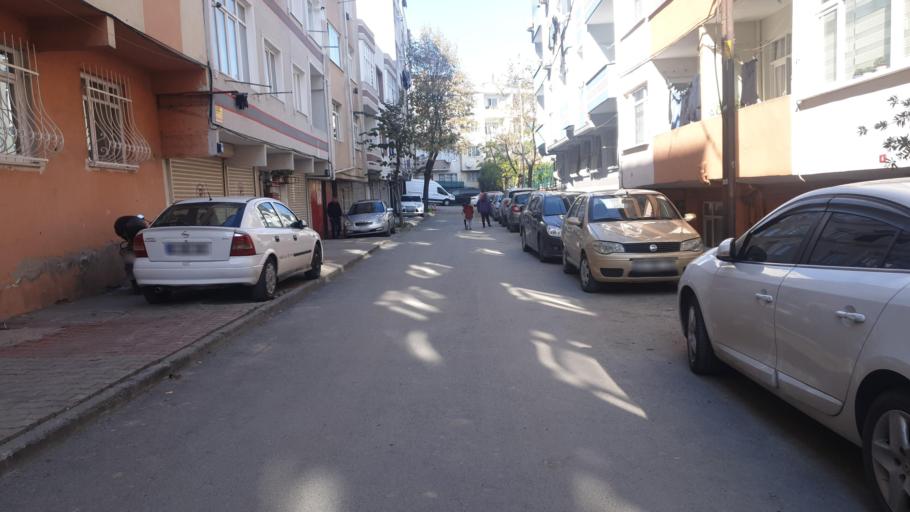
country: TR
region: Istanbul
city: Esenler
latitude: 41.0698
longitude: 28.9023
